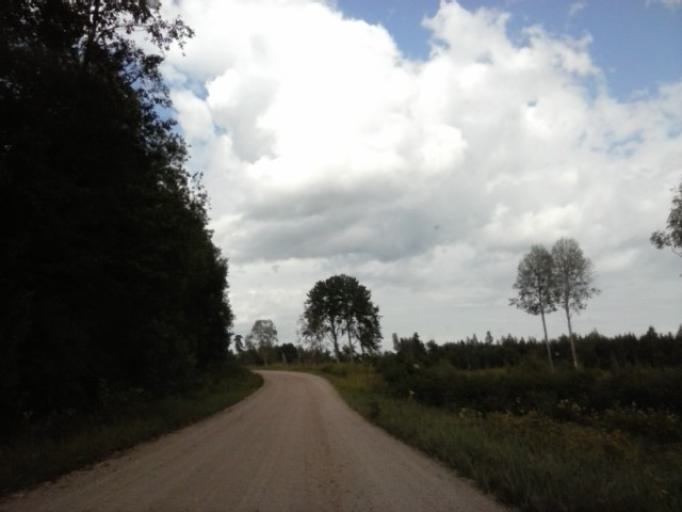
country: EE
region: Vorumaa
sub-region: Voru linn
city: Voru
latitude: 57.7615
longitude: 27.1390
